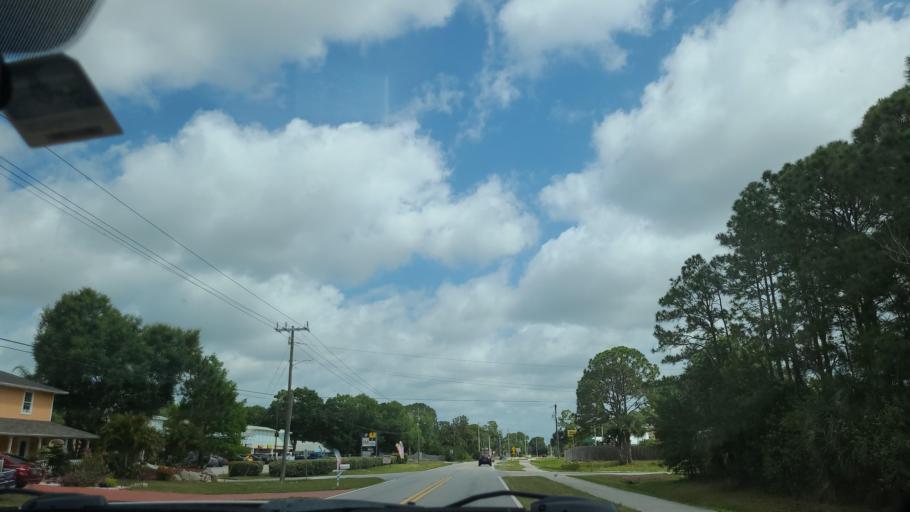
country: US
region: Florida
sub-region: Brevard County
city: June Park
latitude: 28.0207
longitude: -80.6967
